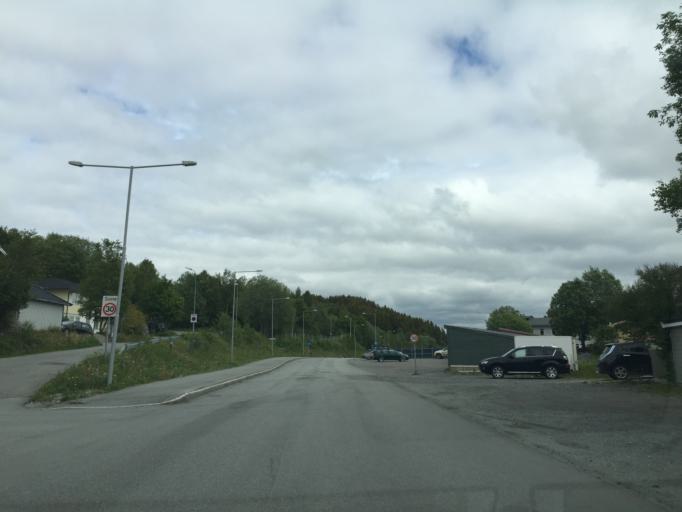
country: NO
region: Nordland
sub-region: Bodo
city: Lopsmarka
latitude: 67.2847
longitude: 14.5360
